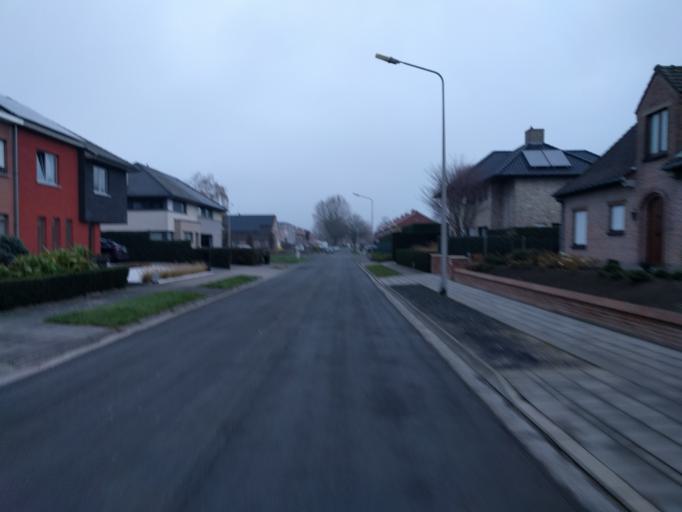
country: BE
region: Flanders
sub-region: Provincie West-Vlaanderen
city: Kortrijk
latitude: 50.8280
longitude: 3.2277
